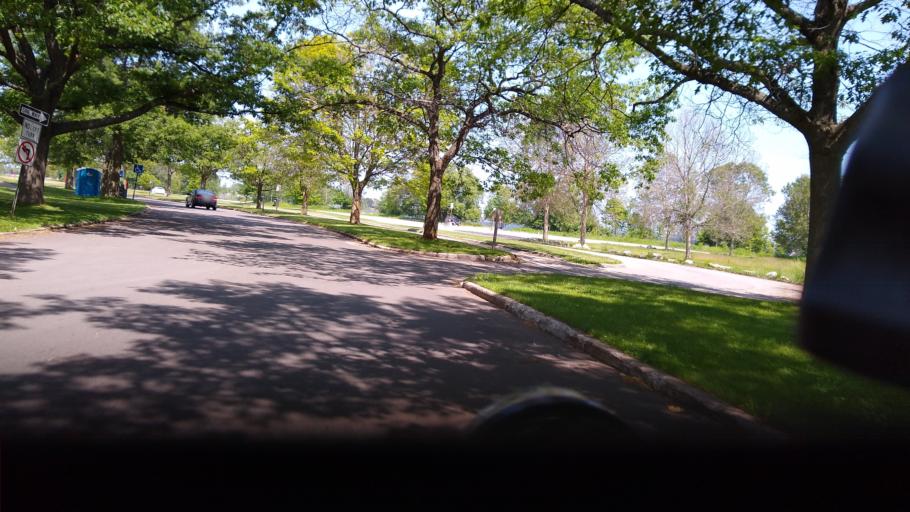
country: US
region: Michigan
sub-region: Delta County
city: Escanaba
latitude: 45.7374
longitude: -87.0565
